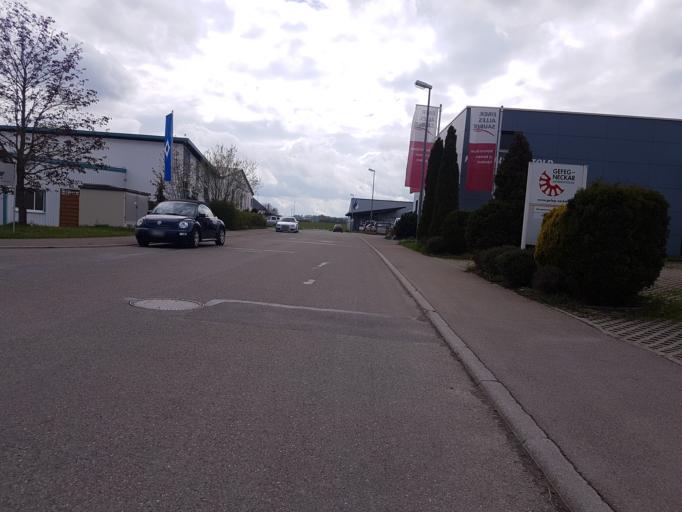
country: DE
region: Baden-Wuerttemberg
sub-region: Freiburg Region
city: Deisslingen
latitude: 48.1059
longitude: 8.5985
